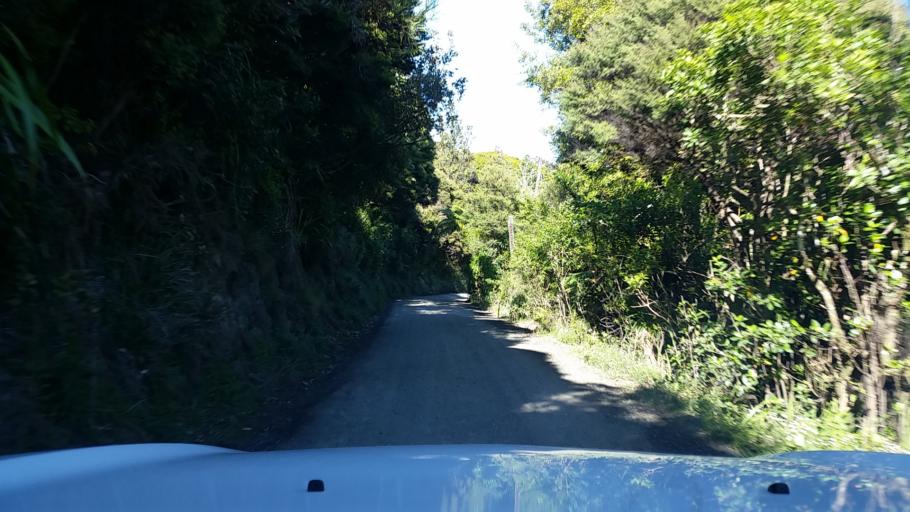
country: NZ
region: Auckland
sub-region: Auckland
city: Titirangi
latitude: -37.0279
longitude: 174.5285
